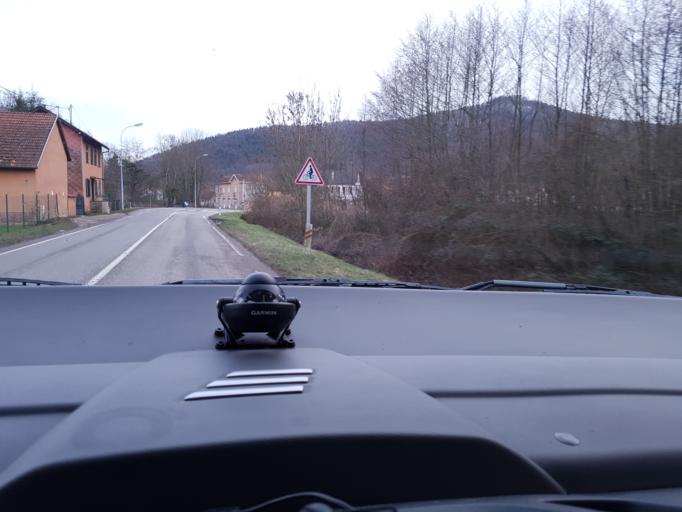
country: FR
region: Alsace
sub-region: Departement du Bas-Rhin
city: Chatenois
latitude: 48.2846
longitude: 7.3814
